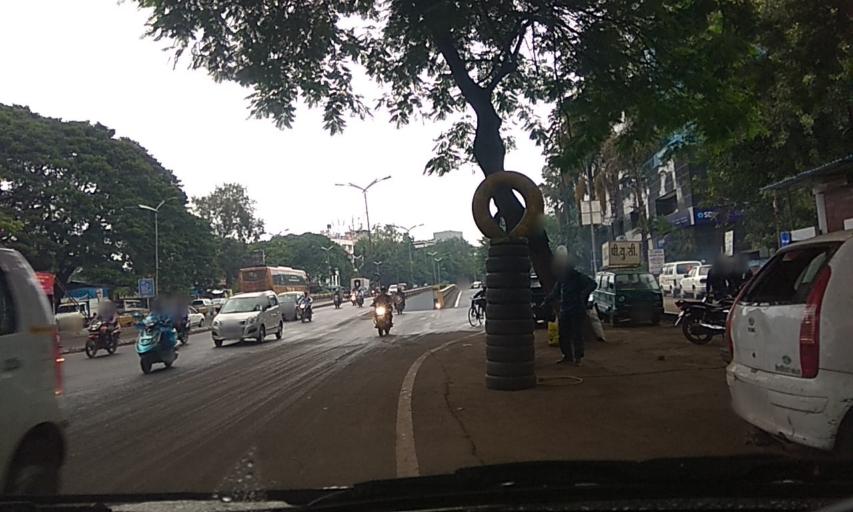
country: IN
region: Maharashtra
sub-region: Pune Division
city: Shivaji Nagar
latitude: 18.5359
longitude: 73.8511
